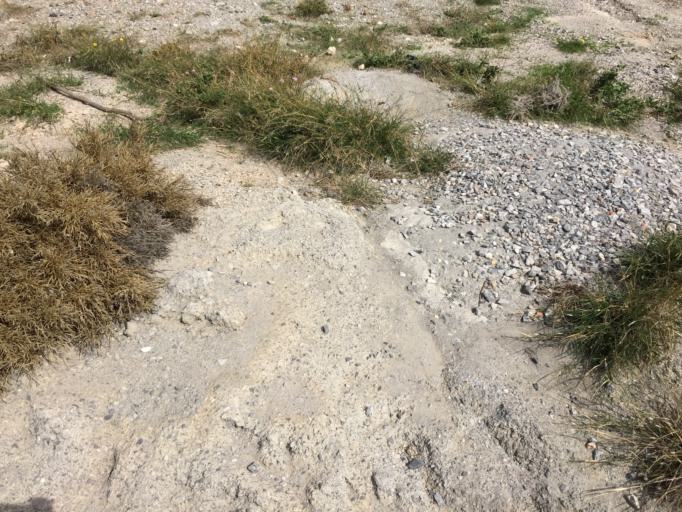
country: GR
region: Crete
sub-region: Nomos Rethymnis
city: Agia Foteini
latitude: 35.1699
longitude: 24.5109
